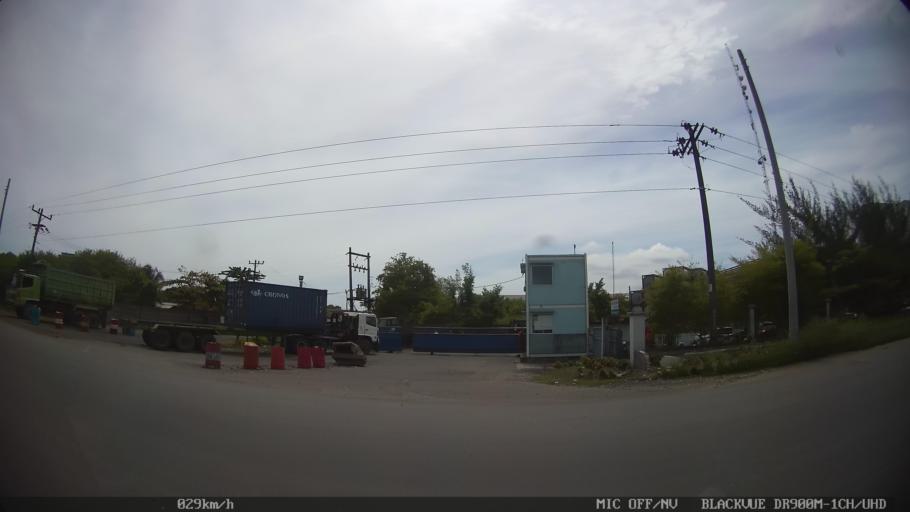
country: ID
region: North Sumatra
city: Belawan
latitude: 3.7737
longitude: 98.6864
